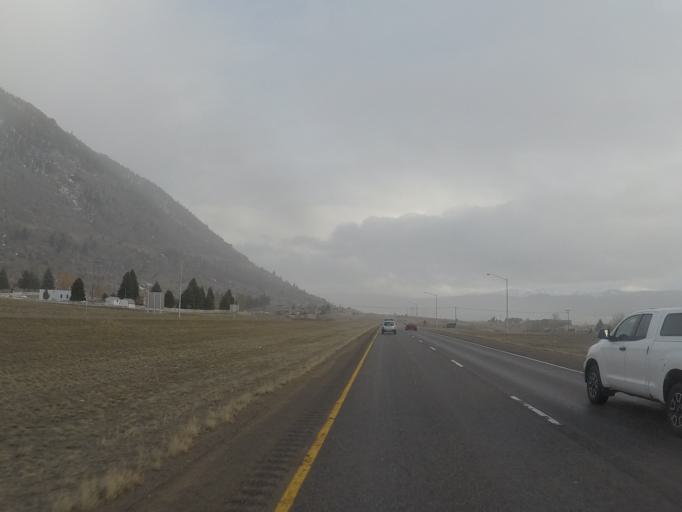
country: US
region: Montana
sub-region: Silver Bow County
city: Butte
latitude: 45.9594
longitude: -112.4713
